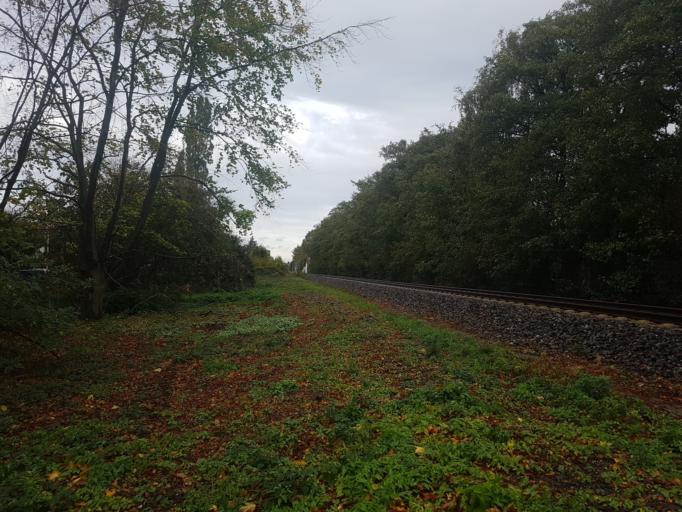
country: DE
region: North Rhine-Westphalia
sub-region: Regierungsbezirk Koln
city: Alsdorf
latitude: 50.8599
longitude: 6.1921
